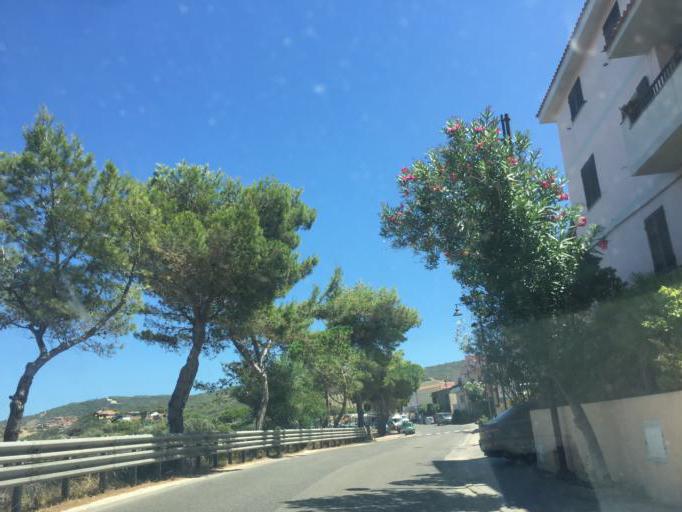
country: IT
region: Sardinia
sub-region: Provincia di Sassari
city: Castelsardo
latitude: 40.9124
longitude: 8.7166
